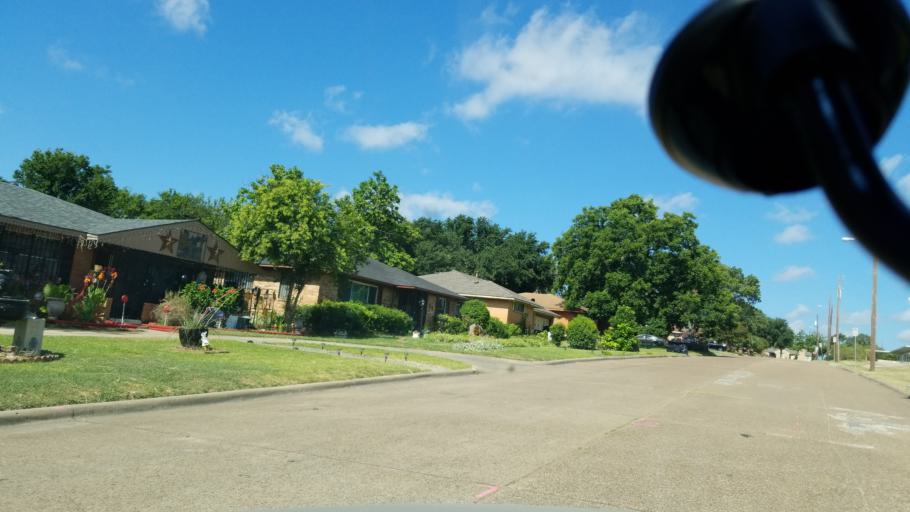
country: US
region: Texas
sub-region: Dallas County
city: Cockrell Hill
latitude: 32.6773
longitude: -96.8121
